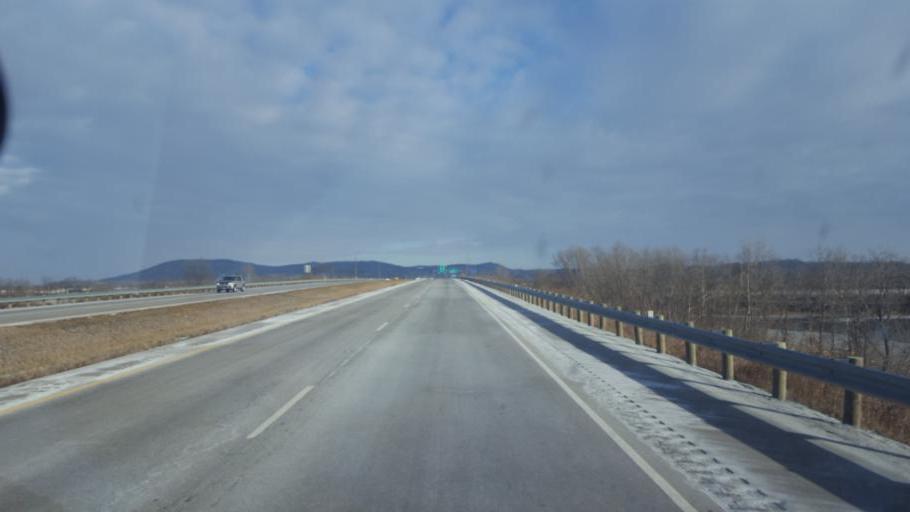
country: US
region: Ohio
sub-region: Ross County
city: Chillicothe
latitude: 39.3074
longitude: -82.9407
